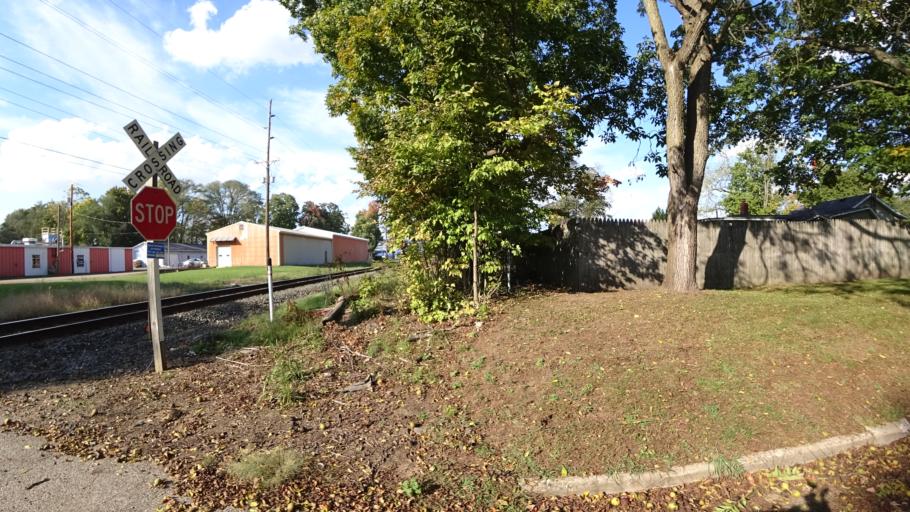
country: US
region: Michigan
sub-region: Saint Joseph County
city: Three Rivers
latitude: 41.9537
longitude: -85.6392
